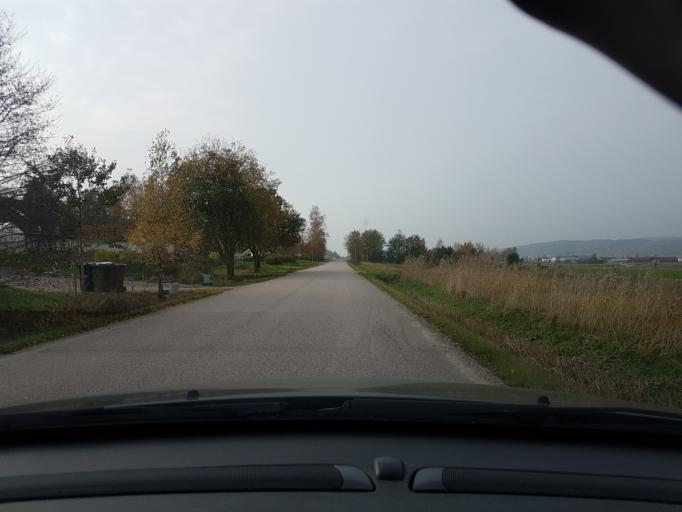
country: SE
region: Vaestra Goetaland
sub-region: Ale Kommun
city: Alvangen
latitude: 57.9678
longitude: 12.1576
